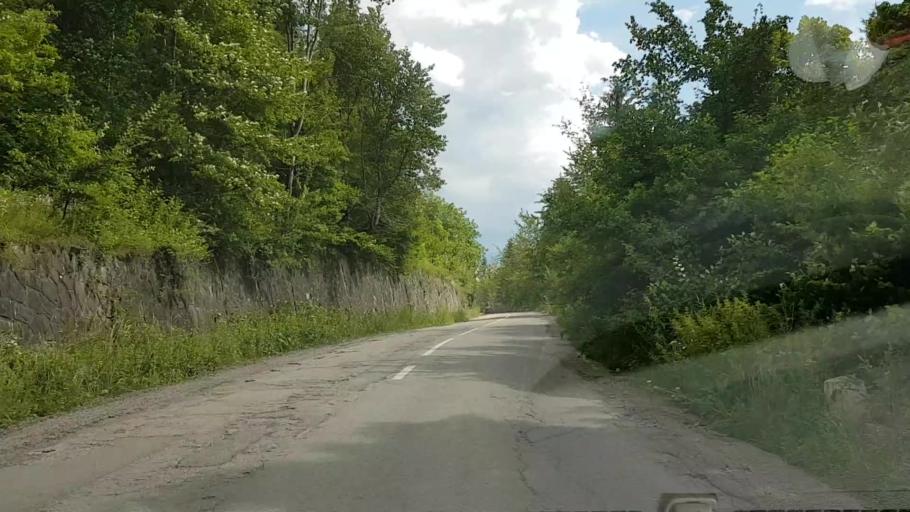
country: RO
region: Neamt
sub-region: Comuna Hangu
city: Hangu
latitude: 47.0543
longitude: 26.0381
